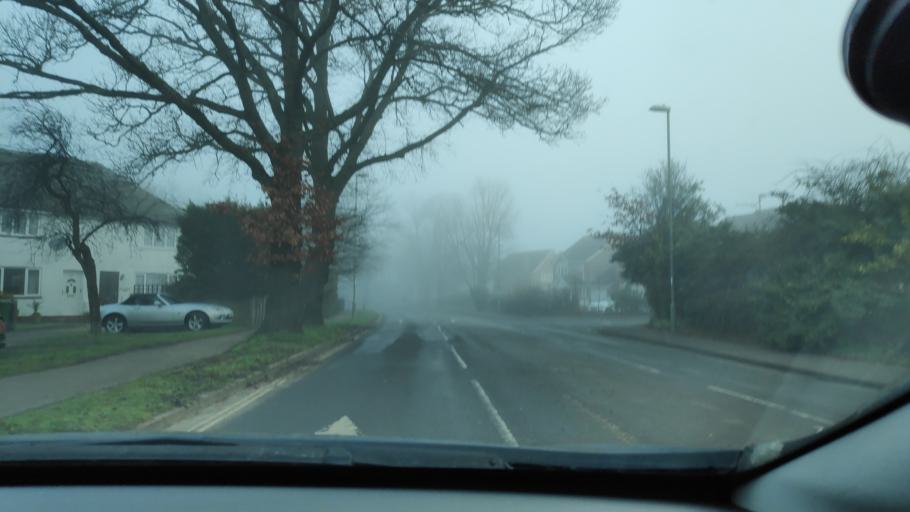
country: GB
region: England
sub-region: Hampshire
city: Farnborough
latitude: 51.2832
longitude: -0.7377
